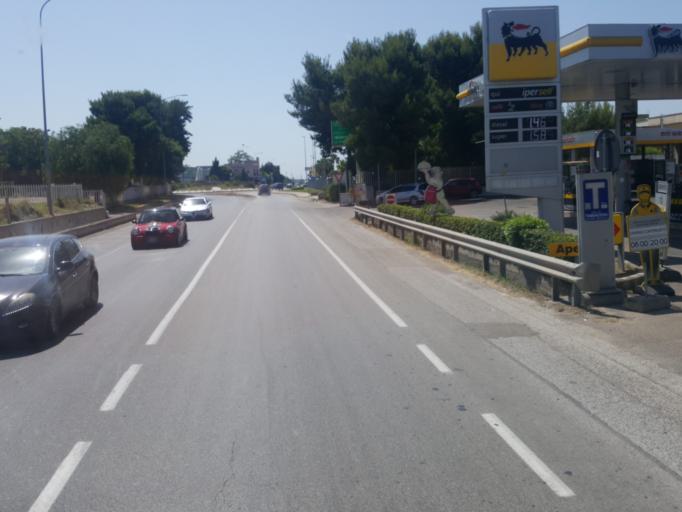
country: IT
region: Apulia
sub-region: Provincia di Taranto
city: Massafra
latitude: 40.5838
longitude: 17.1107
